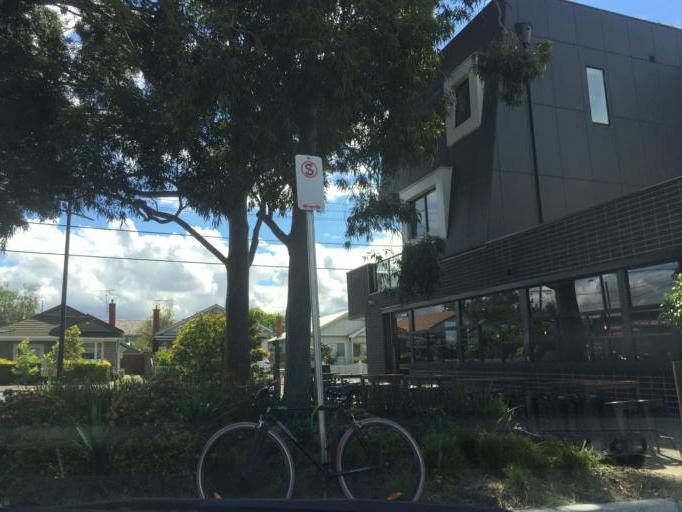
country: AU
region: Victoria
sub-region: Maribyrnong
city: West Footscray
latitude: -37.7983
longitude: 144.8816
